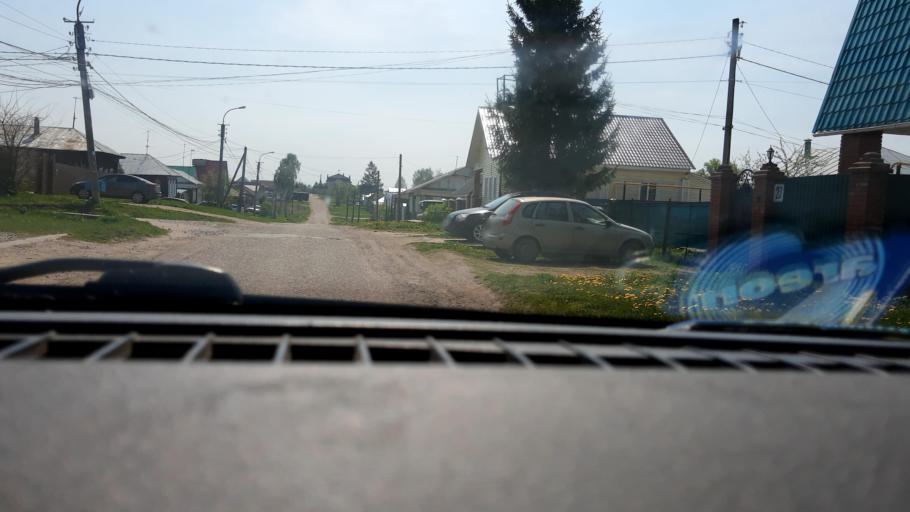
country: RU
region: Bashkortostan
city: Blagoveshchensk
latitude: 55.0255
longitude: 55.9805
